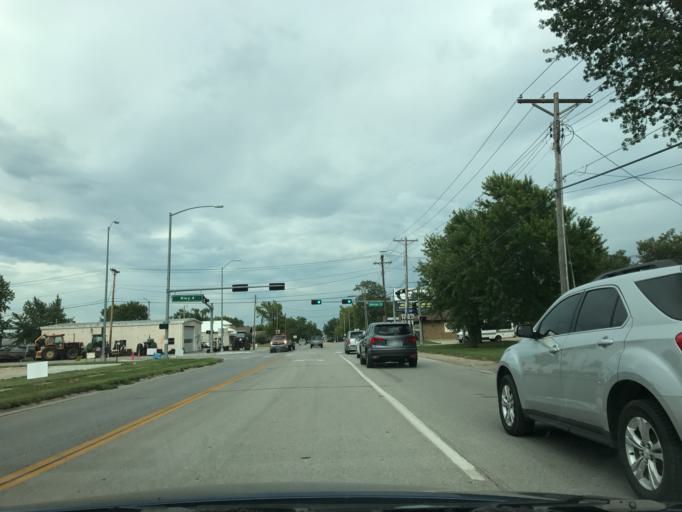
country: US
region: Nebraska
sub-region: Gage County
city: Beatrice
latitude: 40.2656
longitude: -96.7761
